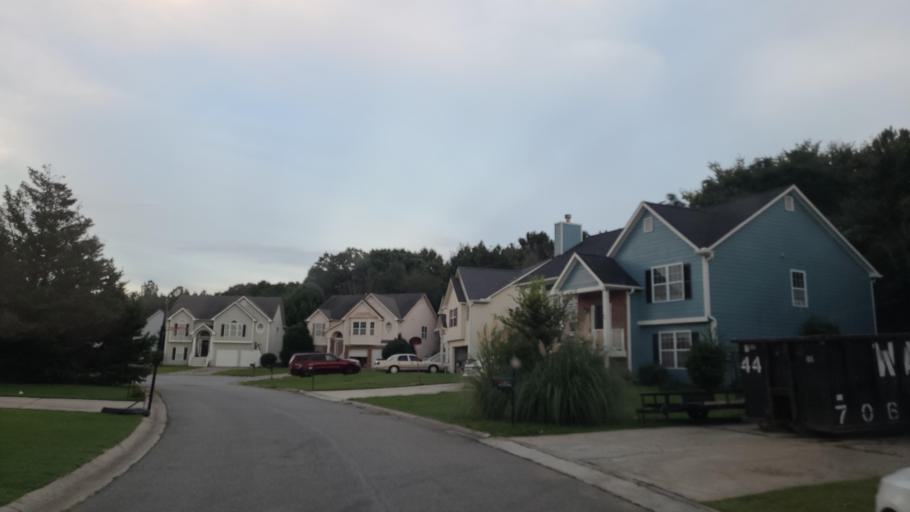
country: US
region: Georgia
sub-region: Bartow County
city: Cartersville
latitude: 34.2115
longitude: -84.7897
